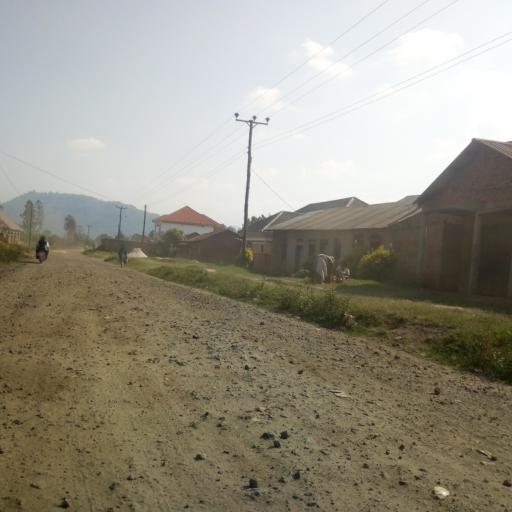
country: UG
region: Western Region
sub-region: Kisoro District
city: Kisoro
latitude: -1.2366
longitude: 29.7130
